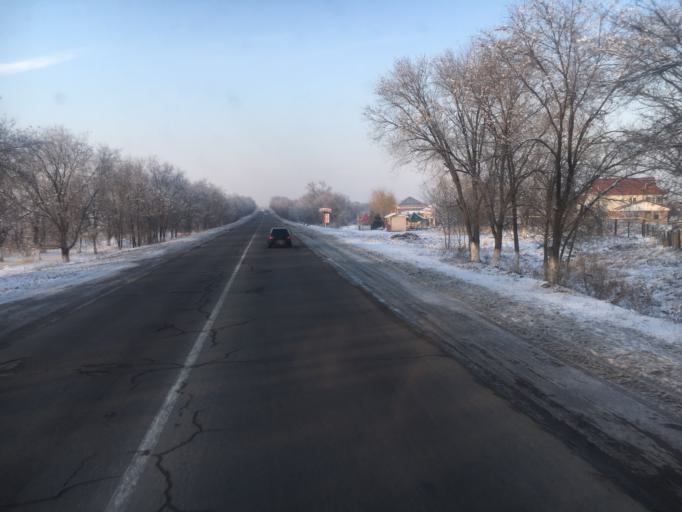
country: KZ
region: Almaty Oblysy
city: Burunday
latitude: 43.3104
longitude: 76.6661
